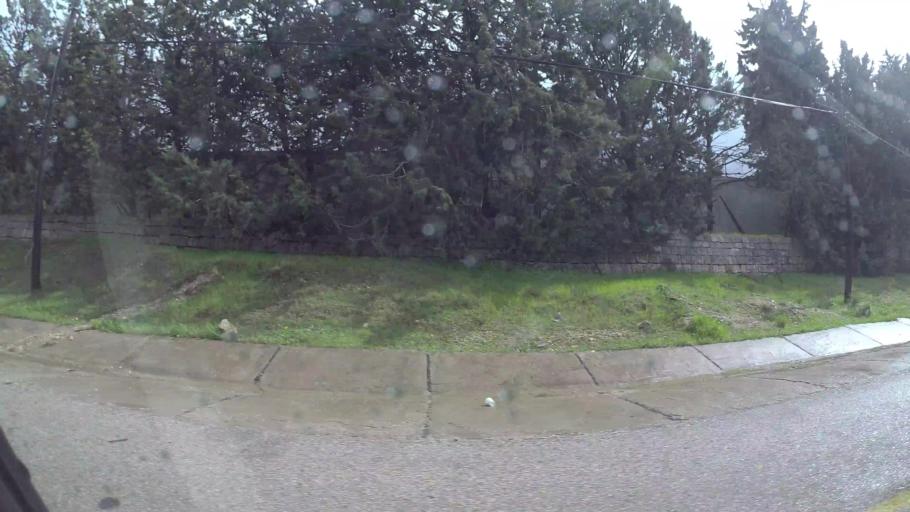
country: JO
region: Amman
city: Al Jubayhah
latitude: 32.0223
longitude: 35.8174
